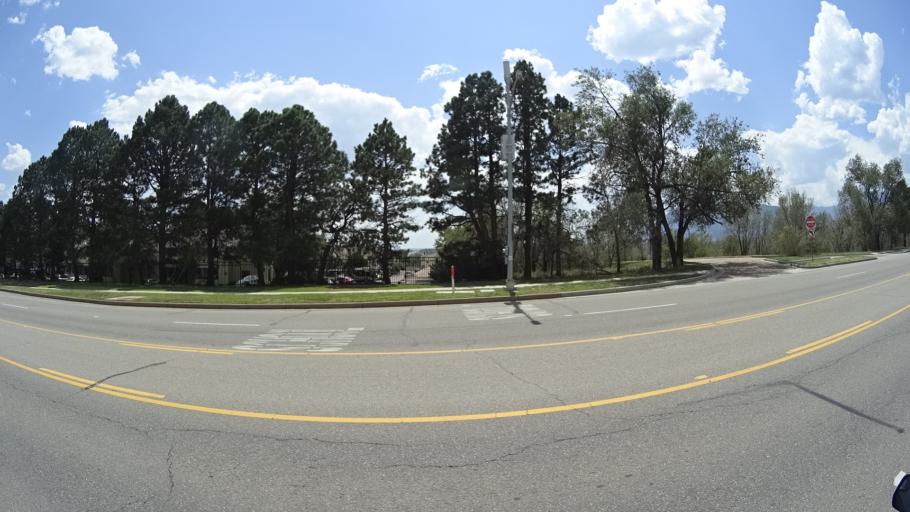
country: US
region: Colorado
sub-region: El Paso County
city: Colorado Springs
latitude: 38.8327
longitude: -104.7817
